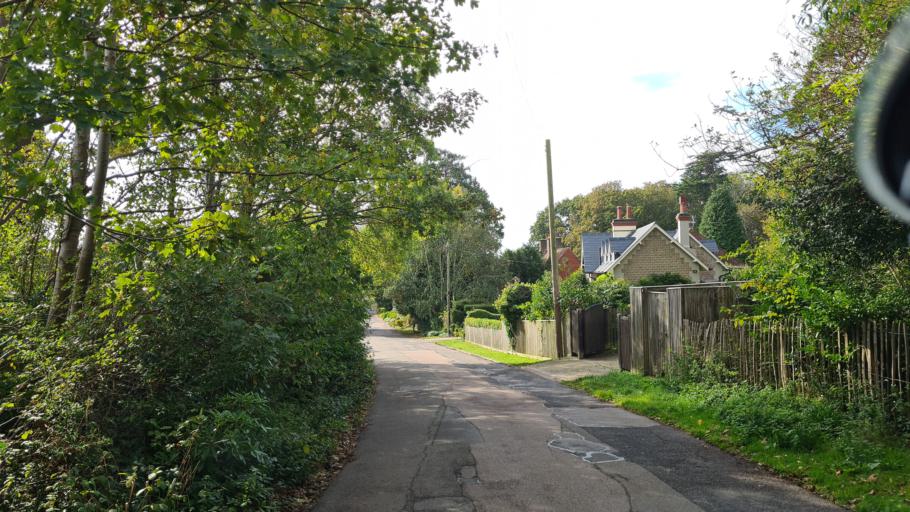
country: GB
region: England
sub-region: East Sussex
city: Hastings
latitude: 50.8797
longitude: 0.5622
